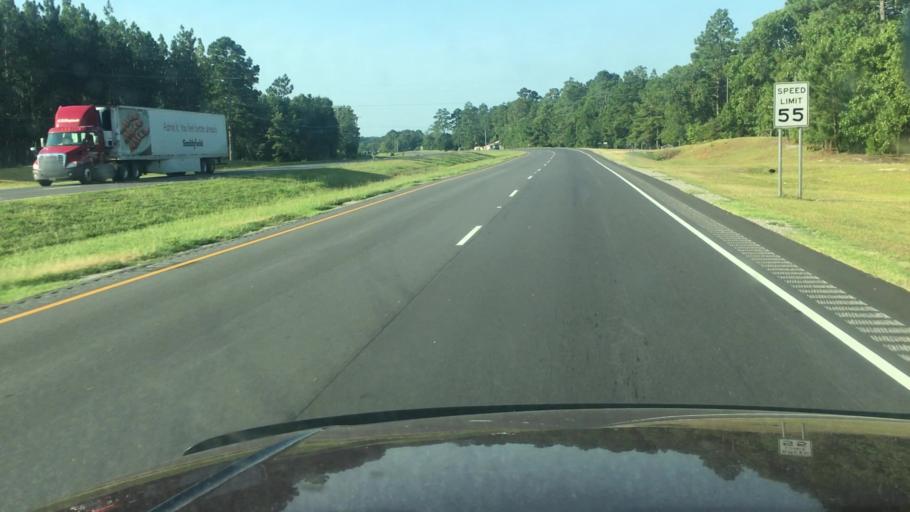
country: US
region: North Carolina
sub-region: Robeson County
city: Saint Pauls
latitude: 34.8693
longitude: -78.8500
